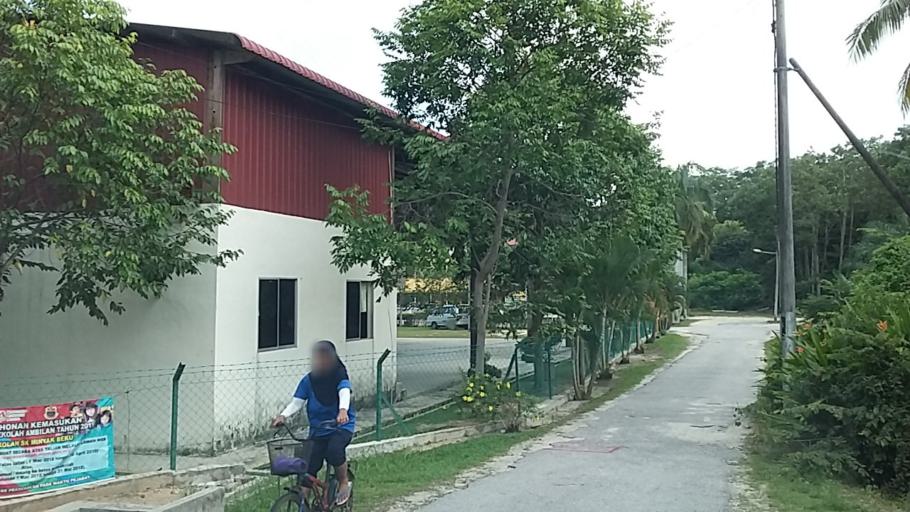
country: MY
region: Johor
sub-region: Daerah Batu Pahat
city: Batu Pahat
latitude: 1.7914
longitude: 102.8938
